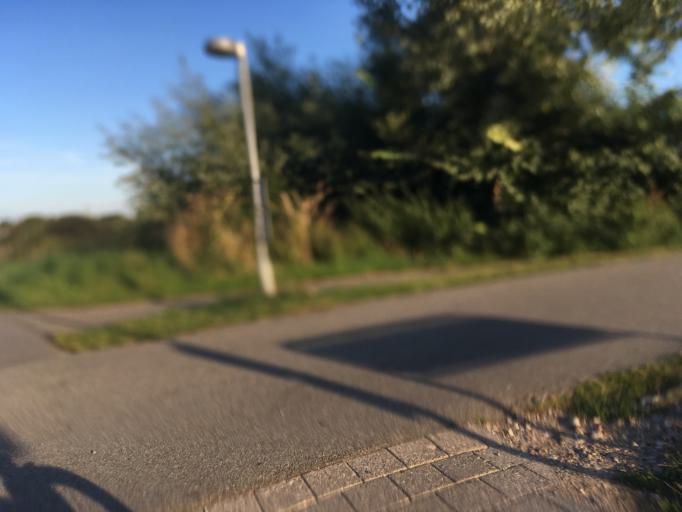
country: DK
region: Capital Region
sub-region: Hillerod Kommune
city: Hillerod
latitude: 55.9291
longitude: 12.2867
